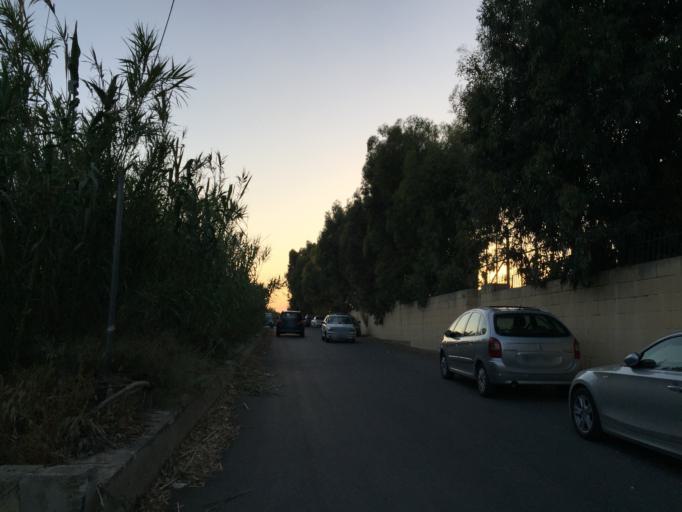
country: MT
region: Il-Marsa
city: Marsa
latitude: 35.8770
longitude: 14.4881
